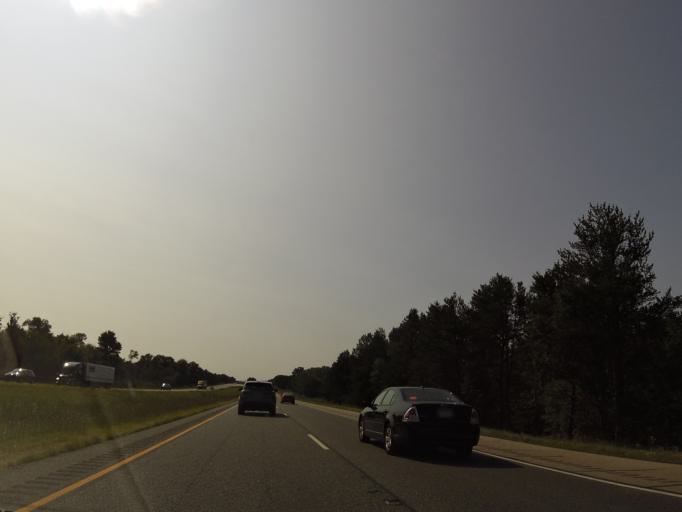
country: US
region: Wisconsin
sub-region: Monroe County
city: Sparta
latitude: 43.9437
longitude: -90.7314
